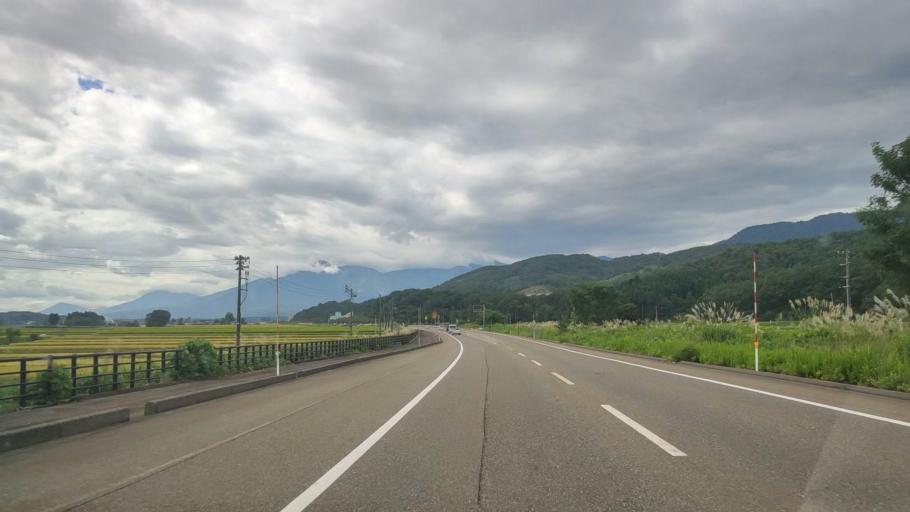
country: JP
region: Niigata
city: Arai
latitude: 37.0476
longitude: 138.2422
